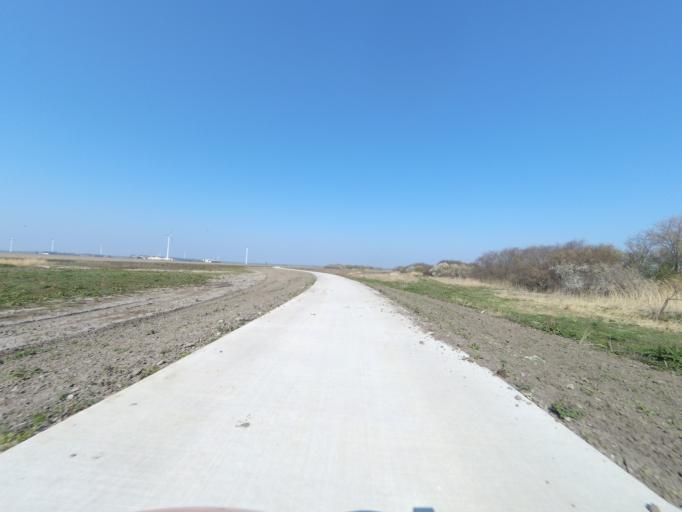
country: NL
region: Utrecht
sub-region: Gemeente Bunschoten
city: Spakenburg
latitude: 52.3720
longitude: 5.3751
